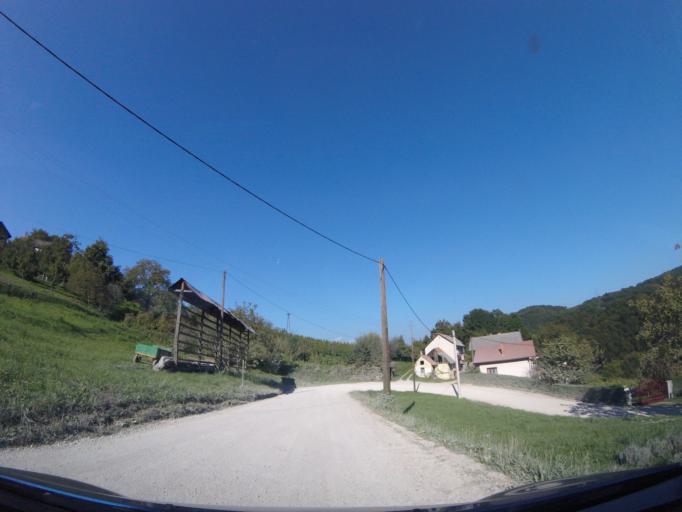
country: HR
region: Zagrebacka
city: Rude
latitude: 45.7593
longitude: 15.6591
